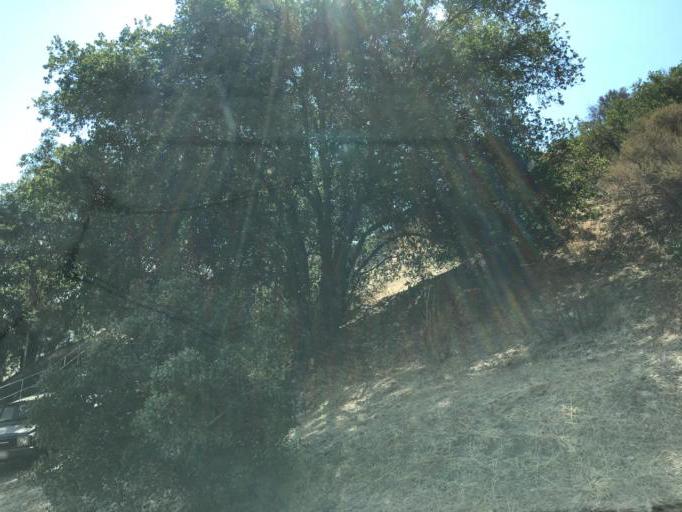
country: US
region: California
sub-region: Los Angeles County
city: Val Verde
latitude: 34.4521
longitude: -118.6659
